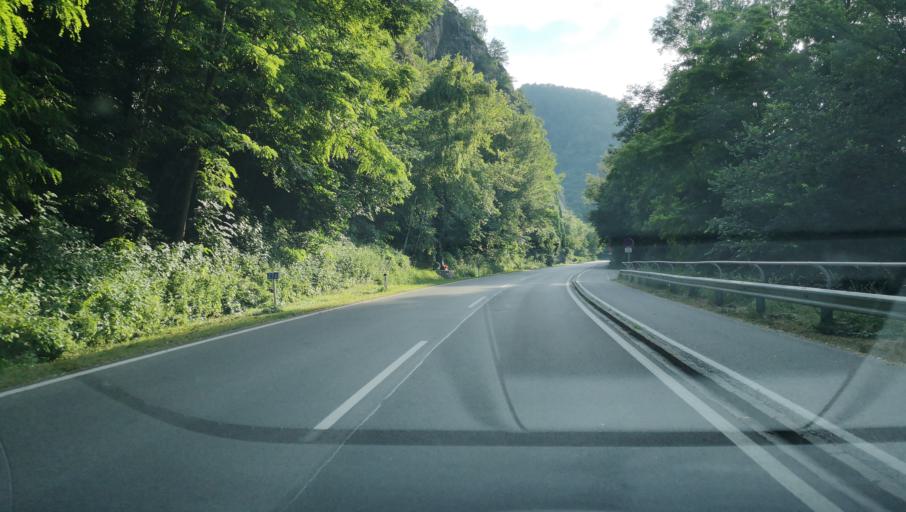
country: AT
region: Lower Austria
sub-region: Politischer Bezirk Krems
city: Durnstein
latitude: 48.3823
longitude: 15.5293
